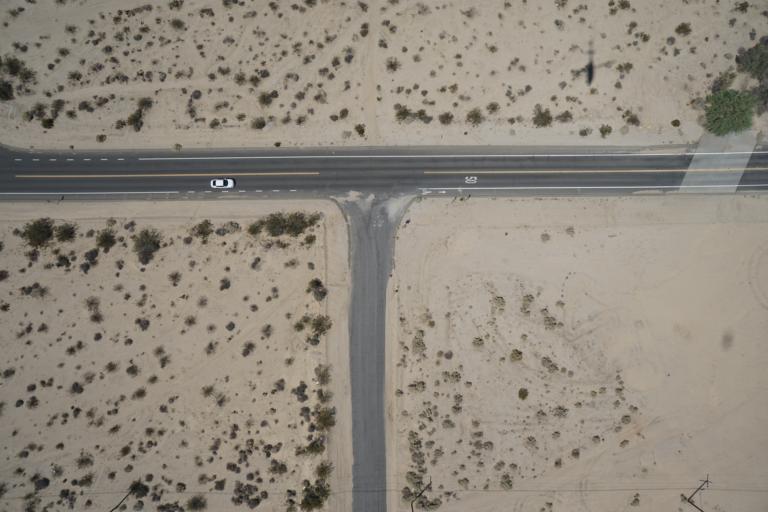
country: US
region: California
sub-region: San Bernardino County
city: Twentynine Palms
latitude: 34.1323
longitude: -116.0364
